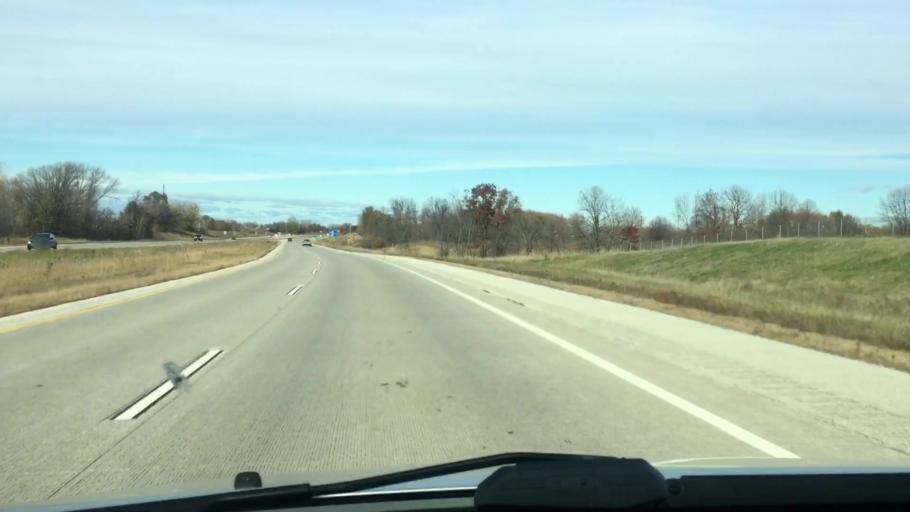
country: US
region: Wisconsin
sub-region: Kewaunee County
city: Luxemburg
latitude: 44.6416
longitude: -87.7530
